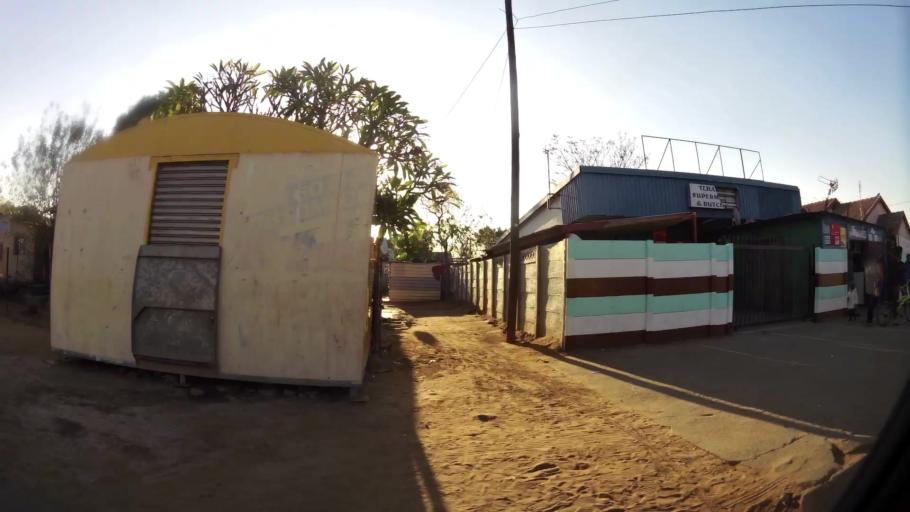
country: ZA
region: North-West
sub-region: Bojanala Platinum District Municipality
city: Rustenburg
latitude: -25.6454
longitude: 27.2182
